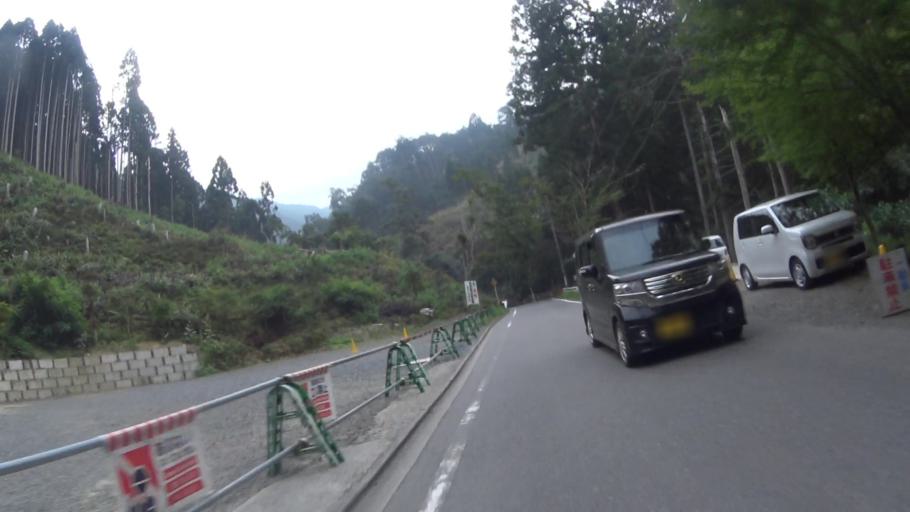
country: JP
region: Kyoto
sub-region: Kyoto-shi
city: Kamigyo-ku
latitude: 35.1079
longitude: 135.7621
